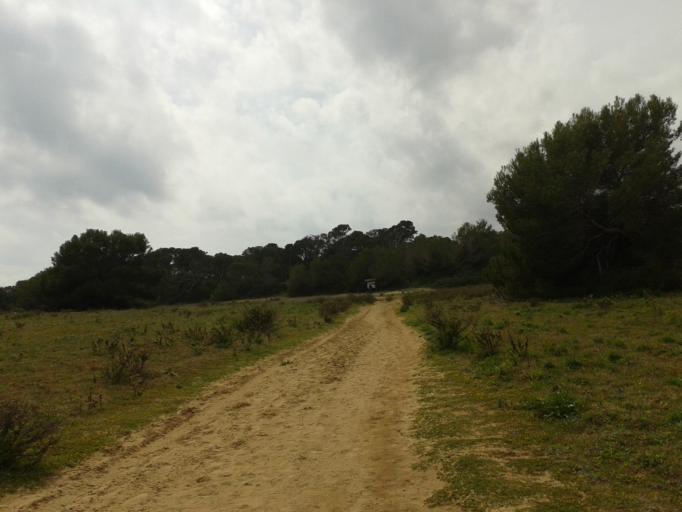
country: ES
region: Balearic Islands
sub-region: Illes Balears
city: Son Servera
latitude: 39.5838
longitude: 3.3900
